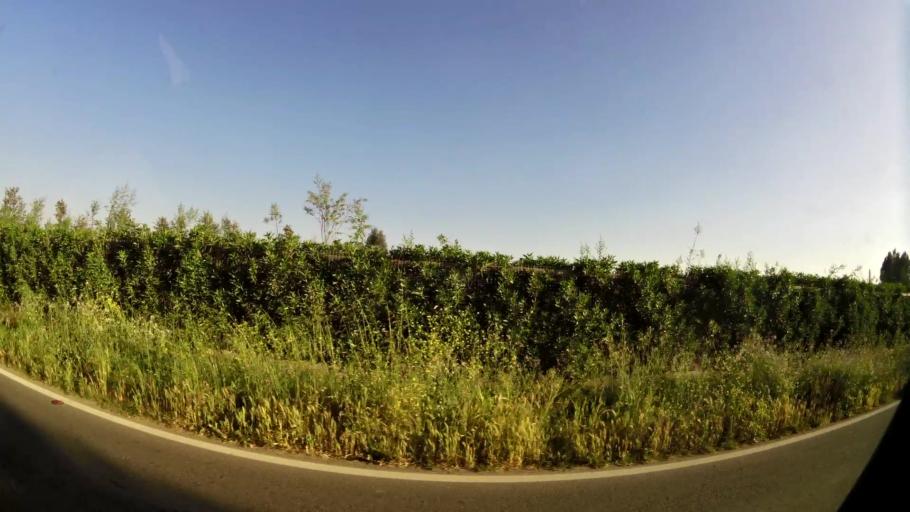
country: CL
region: Santiago Metropolitan
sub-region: Provincia de Talagante
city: Penaflor
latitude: -33.6205
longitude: -70.8701
